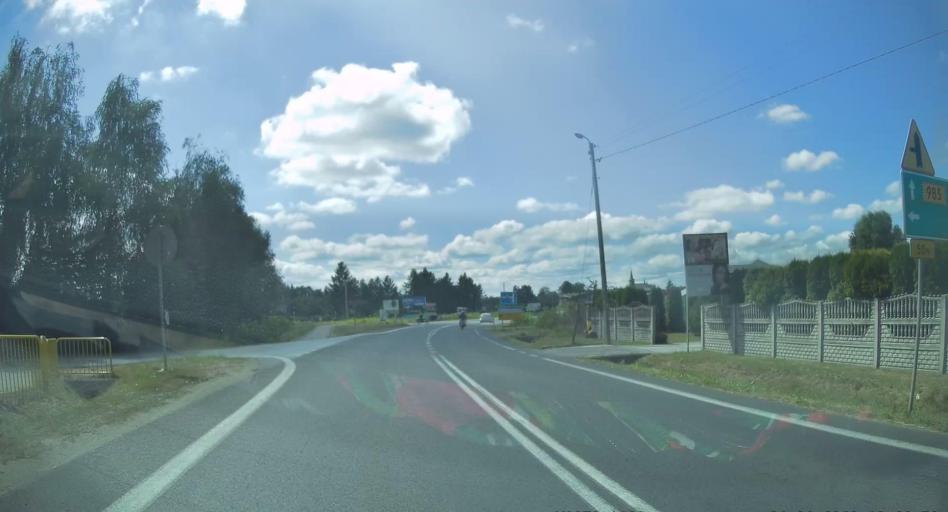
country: PL
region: Subcarpathian Voivodeship
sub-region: Powiat debicki
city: Brzeznica
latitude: 50.1102
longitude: 21.4899
